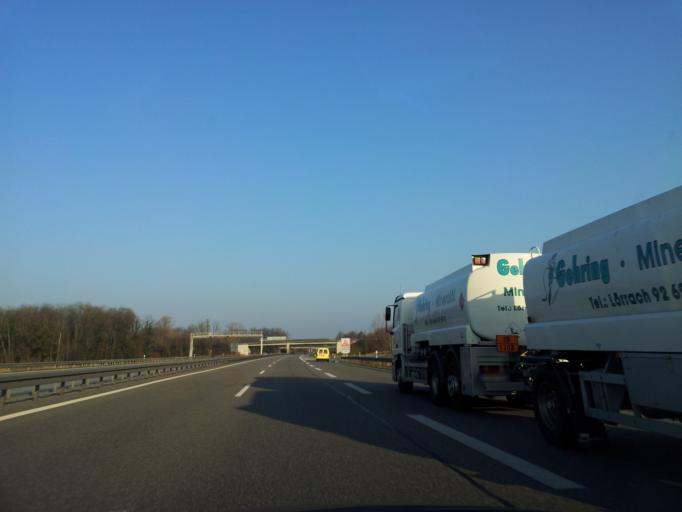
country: FR
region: Alsace
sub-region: Departement du Haut-Rhin
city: Huningue
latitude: 47.6153
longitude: 7.5871
